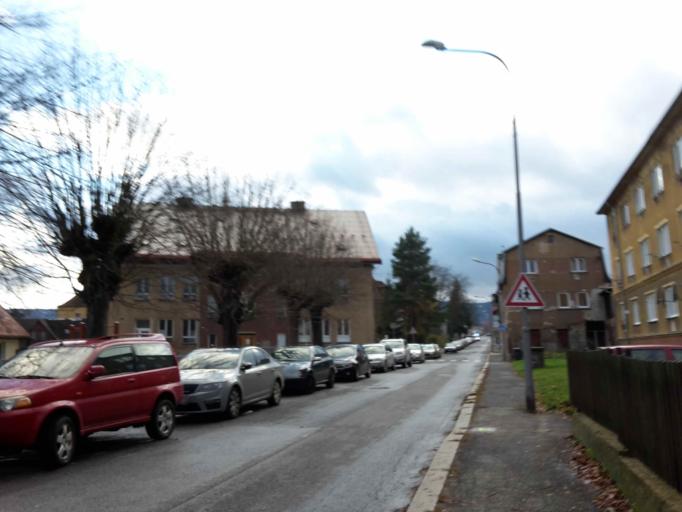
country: CZ
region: Liberecky
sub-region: Okres Liberec
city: Liberec
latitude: 50.7755
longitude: 15.0430
